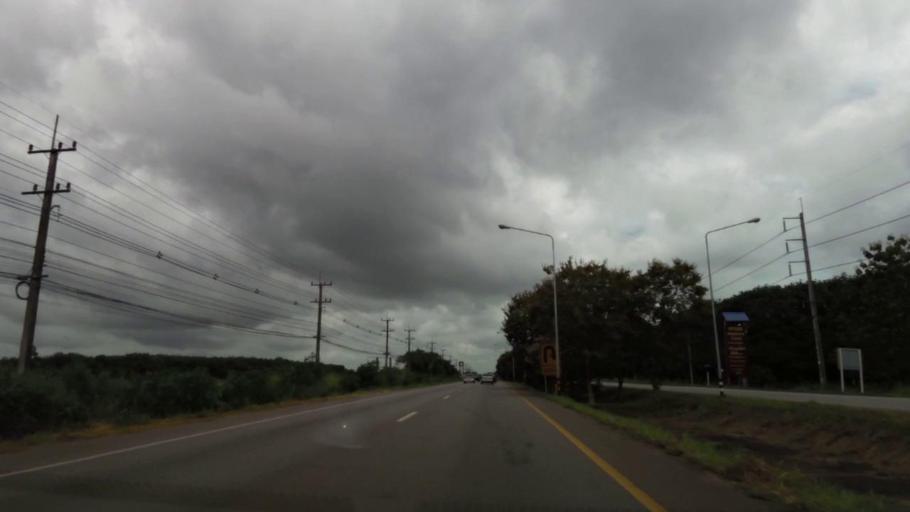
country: TH
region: Chanthaburi
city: Na Yai Am
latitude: 12.7759
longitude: 101.8336
